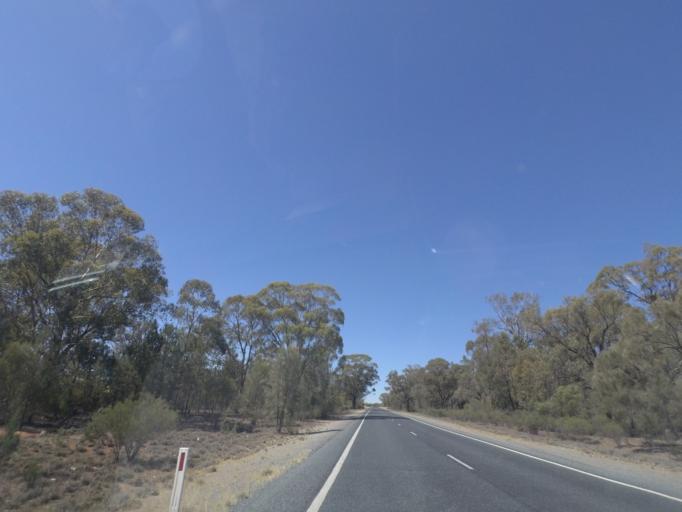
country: AU
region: New South Wales
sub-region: Narrandera
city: Narrandera
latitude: -34.4423
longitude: 146.8409
